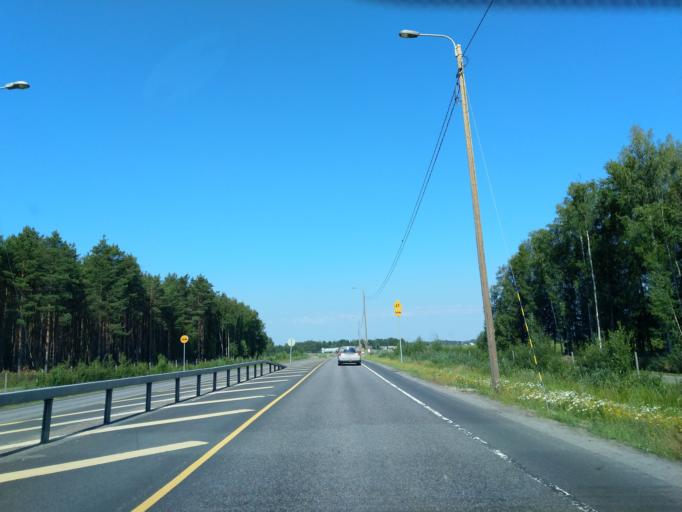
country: FI
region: Satakunta
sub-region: Pori
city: Nakkila
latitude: 61.3449
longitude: 22.0248
